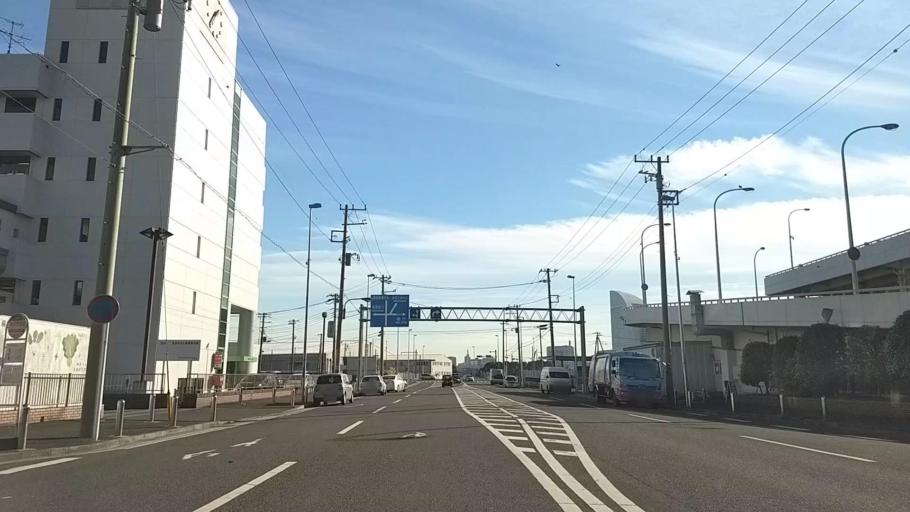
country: JP
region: Kanagawa
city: Yokohama
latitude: 35.4676
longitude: 139.6357
